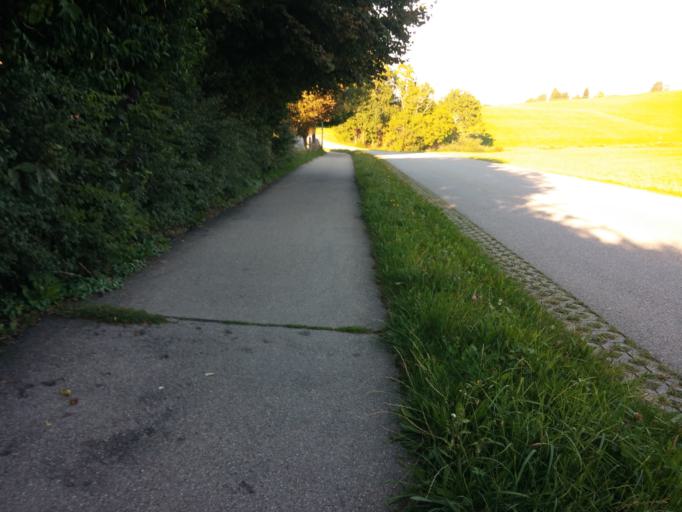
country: DE
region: Bavaria
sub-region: Swabia
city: Wiggensbach
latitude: 47.7444
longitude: 10.2224
